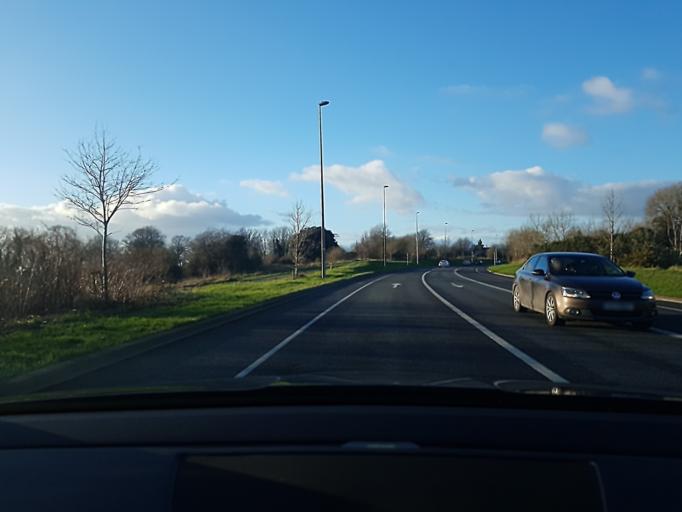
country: IE
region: Munster
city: Moyross
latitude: 52.6613
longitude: -8.6649
